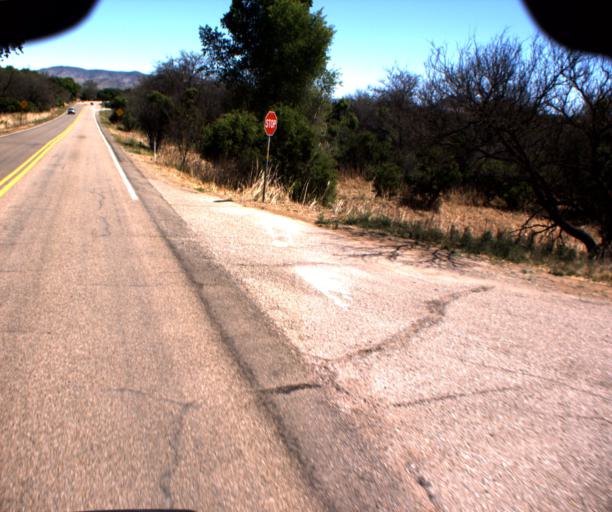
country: US
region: Arizona
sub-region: Santa Cruz County
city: Rio Rico
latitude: 31.5341
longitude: -110.7633
